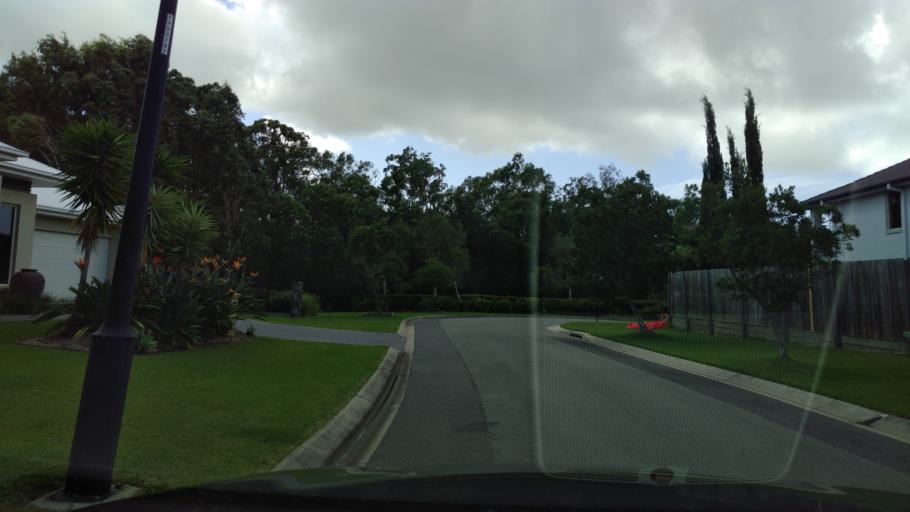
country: AU
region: Queensland
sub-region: Moreton Bay
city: Deception Bay
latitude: -27.2108
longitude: 153.0239
